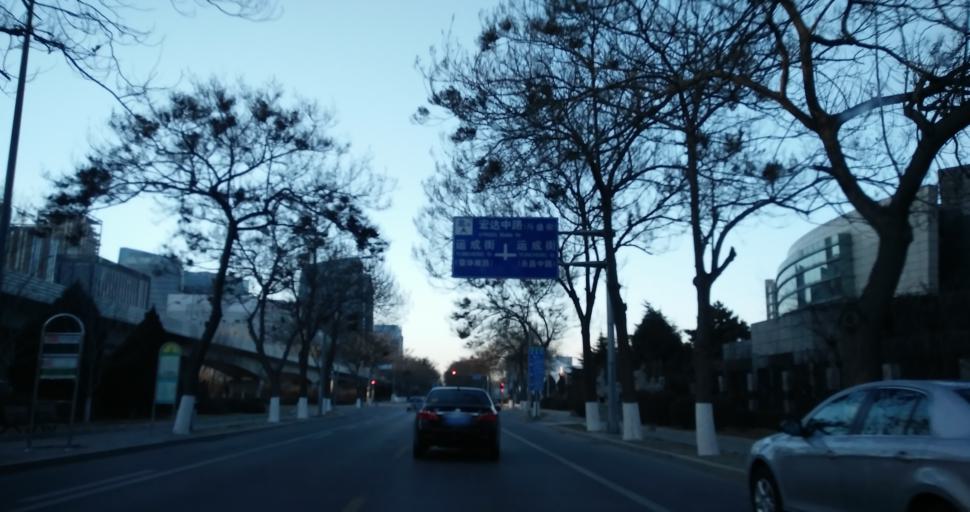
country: CN
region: Beijing
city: Jiugong
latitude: 39.7859
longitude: 116.5128
